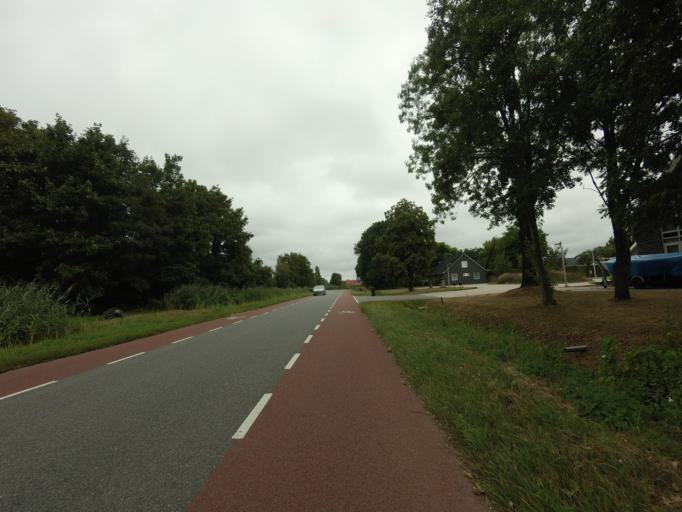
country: NL
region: Gelderland
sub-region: Gemeente Overbetuwe
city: Driel
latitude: 51.9510
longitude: 5.8276
